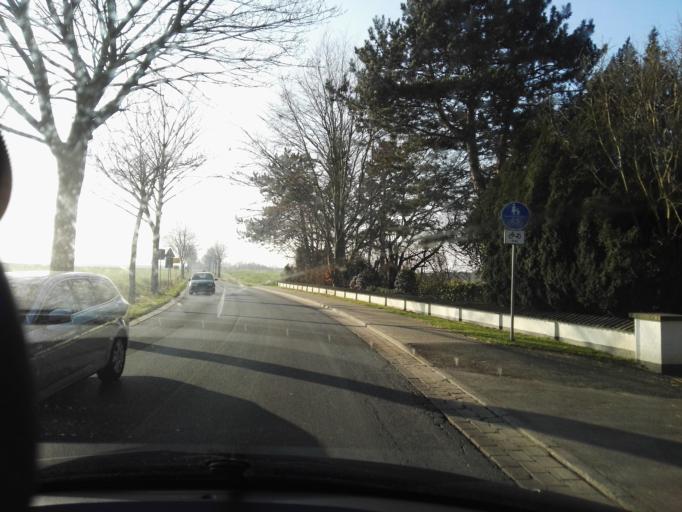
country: DE
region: Lower Saxony
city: Sarstedt
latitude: 52.2123
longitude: 9.8316
